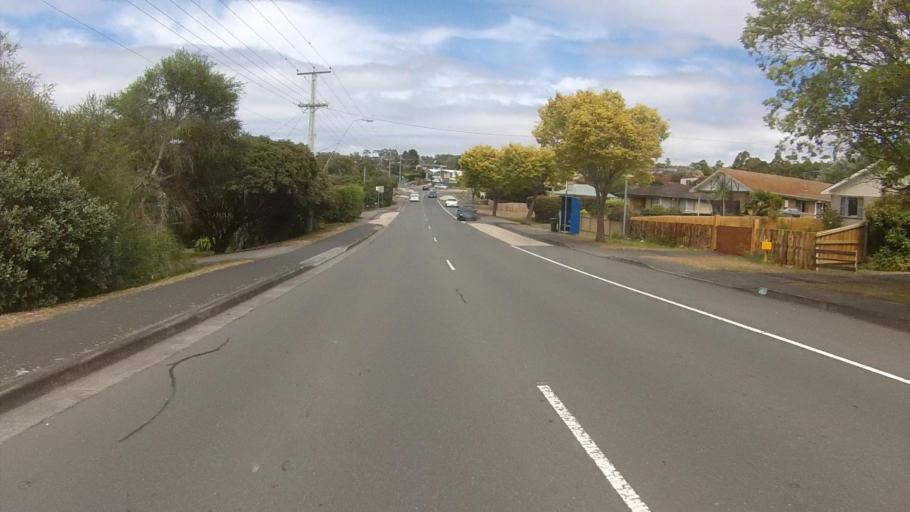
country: AU
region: Tasmania
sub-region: Kingborough
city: Blackmans Bay
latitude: -42.9980
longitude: 147.3220
